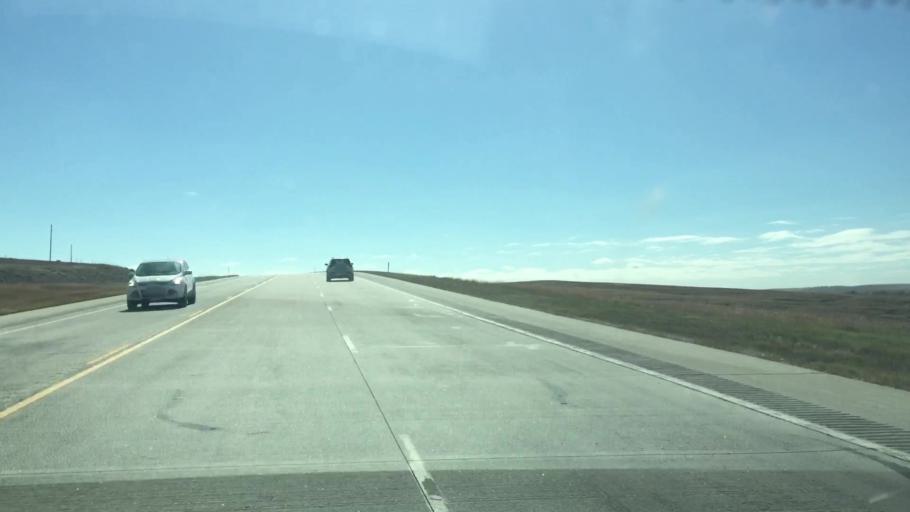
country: US
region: Colorado
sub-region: Lincoln County
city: Limon
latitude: 39.2140
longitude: -103.6011
